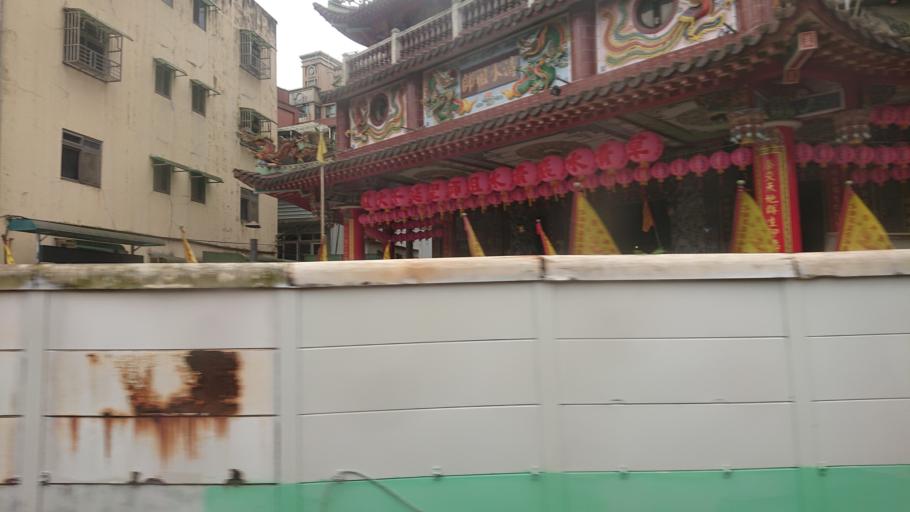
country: TW
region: Taiwan
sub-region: Keelung
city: Keelung
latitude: 25.0896
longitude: 121.7079
